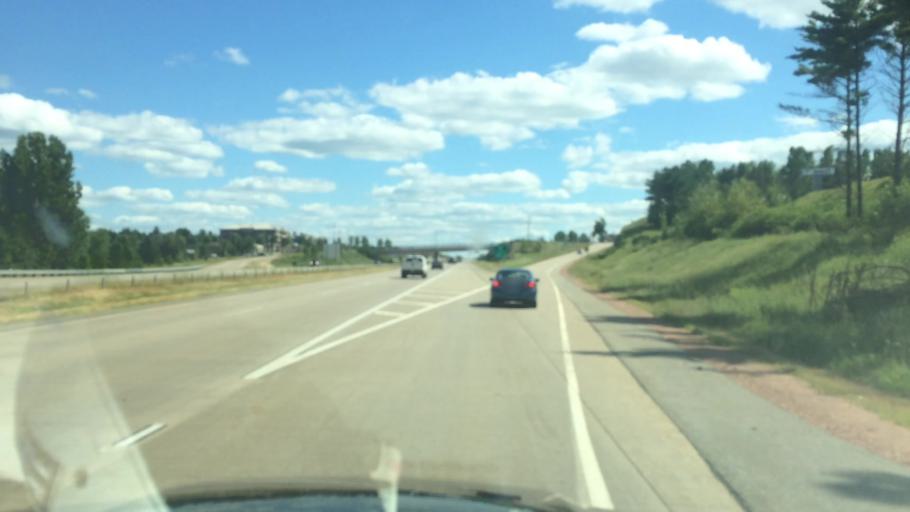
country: US
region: Wisconsin
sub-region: Marathon County
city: Wausau
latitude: 44.9737
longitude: -89.6570
